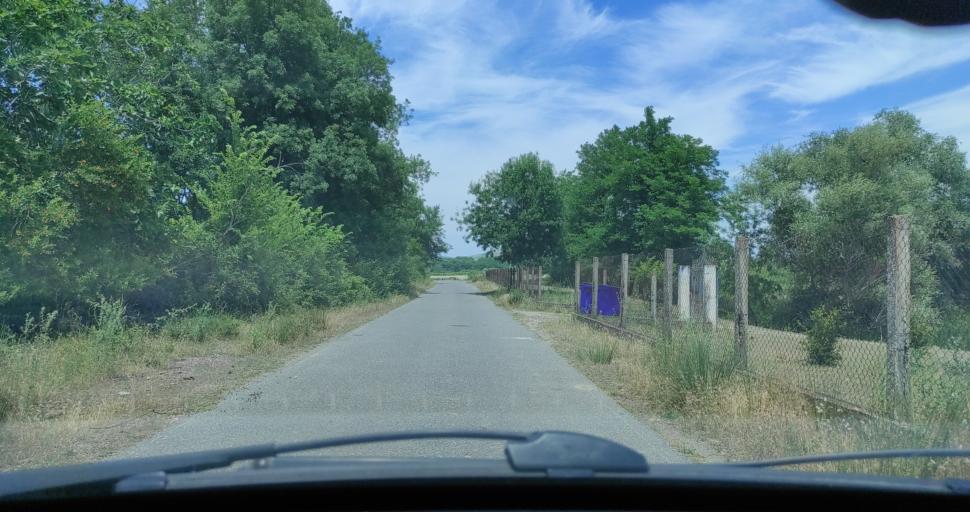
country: AL
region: Shkoder
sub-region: Rrethi i Shkodres
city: Velipoje
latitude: 41.8775
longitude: 19.3839
